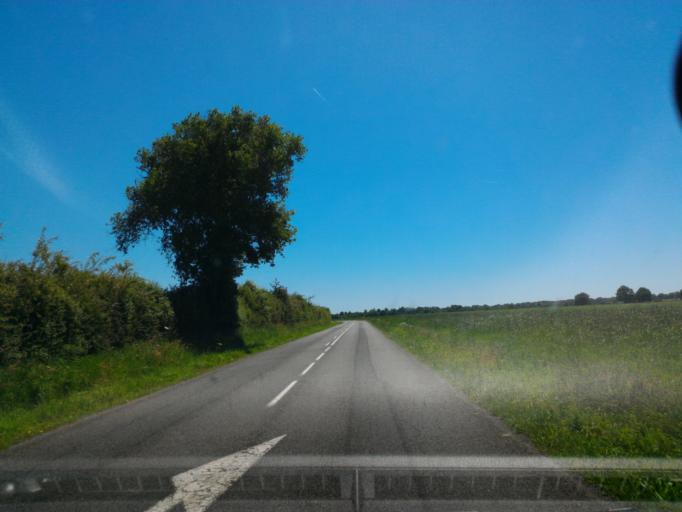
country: FR
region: Poitou-Charentes
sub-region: Departement de la Vienne
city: Availles-Limouzine
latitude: 46.1989
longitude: 0.7093
